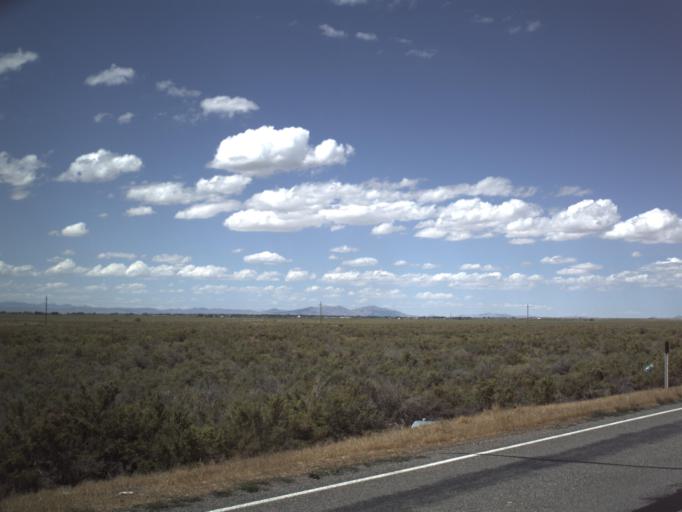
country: US
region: Utah
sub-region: Millard County
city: Delta
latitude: 39.3139
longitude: -112.4785
